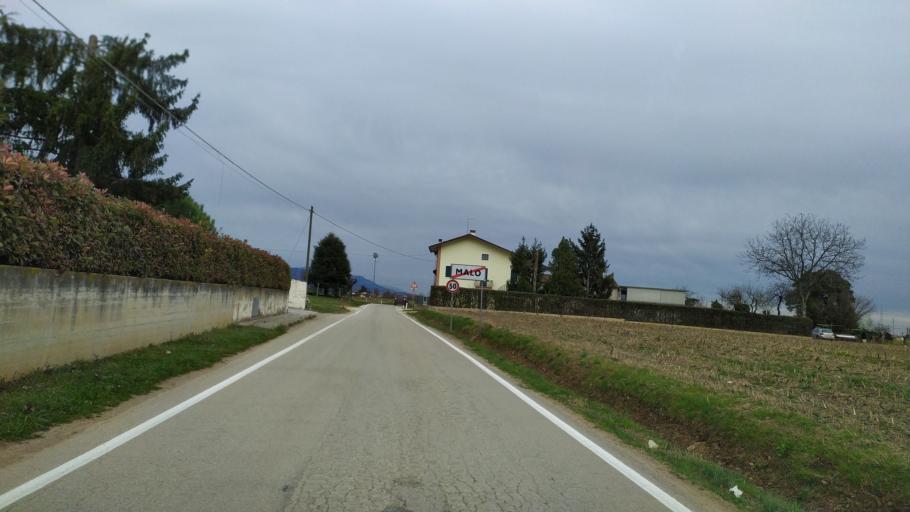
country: IT
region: Veneto
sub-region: Provincia di Vicenza
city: Malo
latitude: 45.6557
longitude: 11.4254
